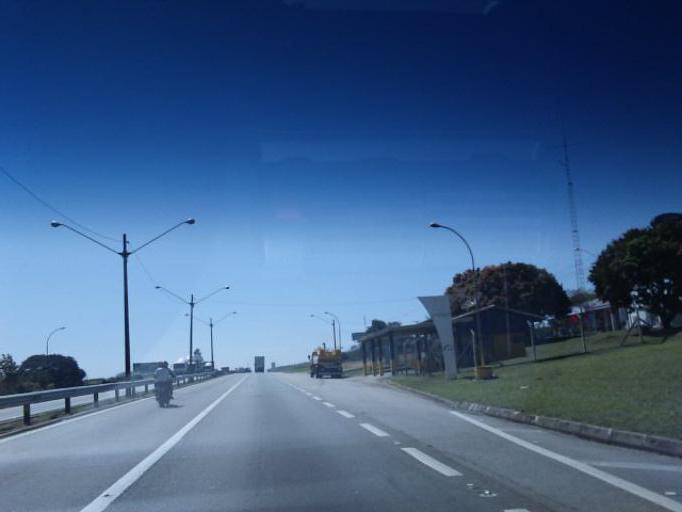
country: BR
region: Sao Paulo
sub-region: Cacapava
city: Cacapava
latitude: -23.1067
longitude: -45.6978
